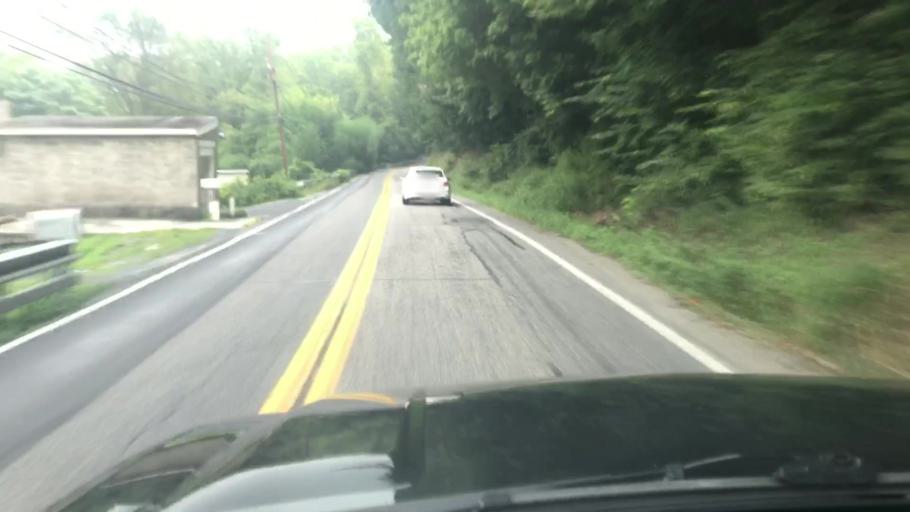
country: US
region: Pennsylvania
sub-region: Cumberland County
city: Shiremanstown
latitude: 40.2497
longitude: -76.9733
